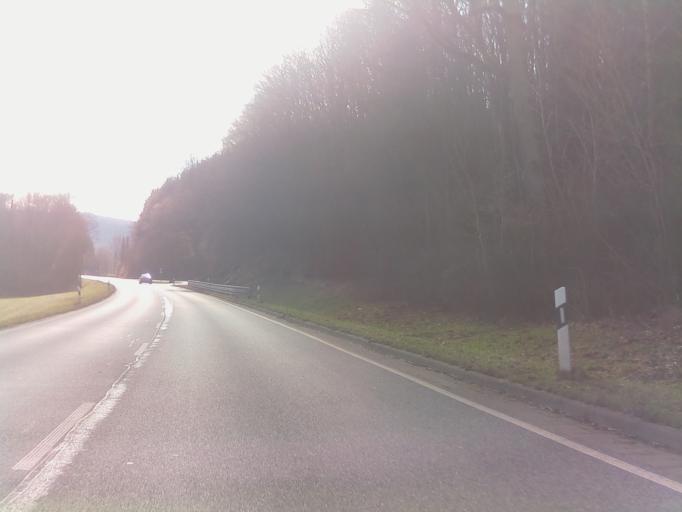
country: DE
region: Hesse
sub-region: Regierungsbezirk Darmstadt
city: Hirzenhain
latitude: 50.3971
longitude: 9.1414
